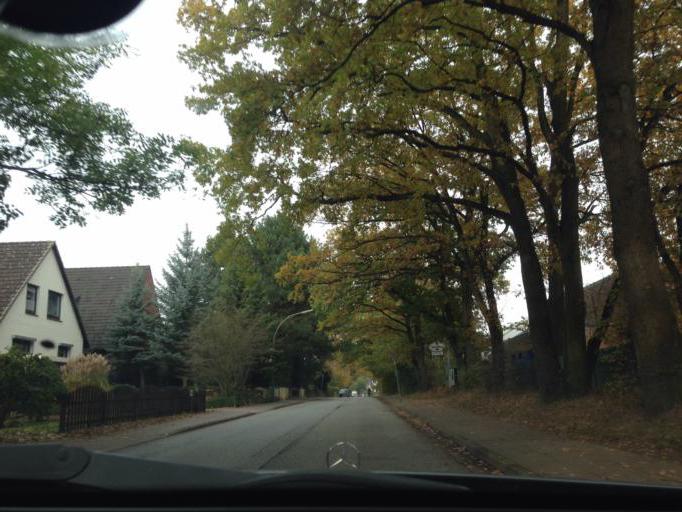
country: DE
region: Schleswig-Holstein
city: Barsbuettel
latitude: 53.5941
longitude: 10.1608
